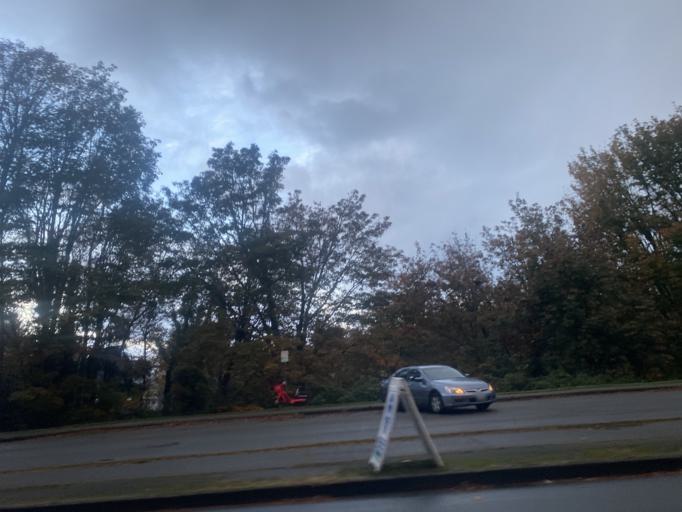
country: US
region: Washington
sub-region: King County
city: Seattle
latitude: 47.6352
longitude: -122.3979
